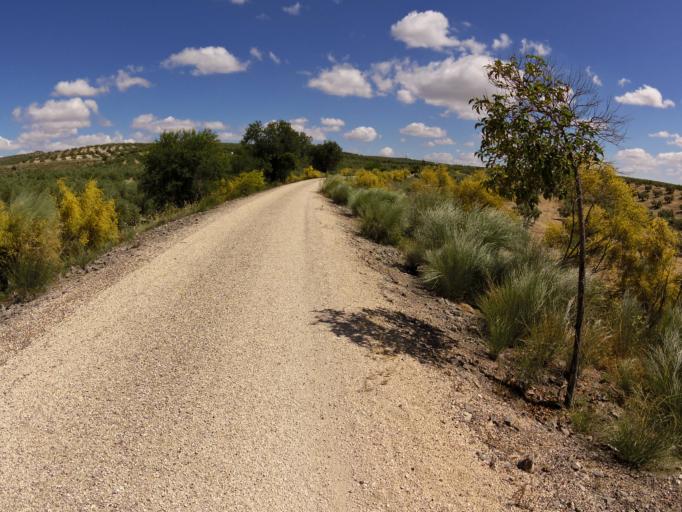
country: ES
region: Andalusia
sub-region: Provincia de Jaen
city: Alcaudete
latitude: 37.6427
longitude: -4.0823
